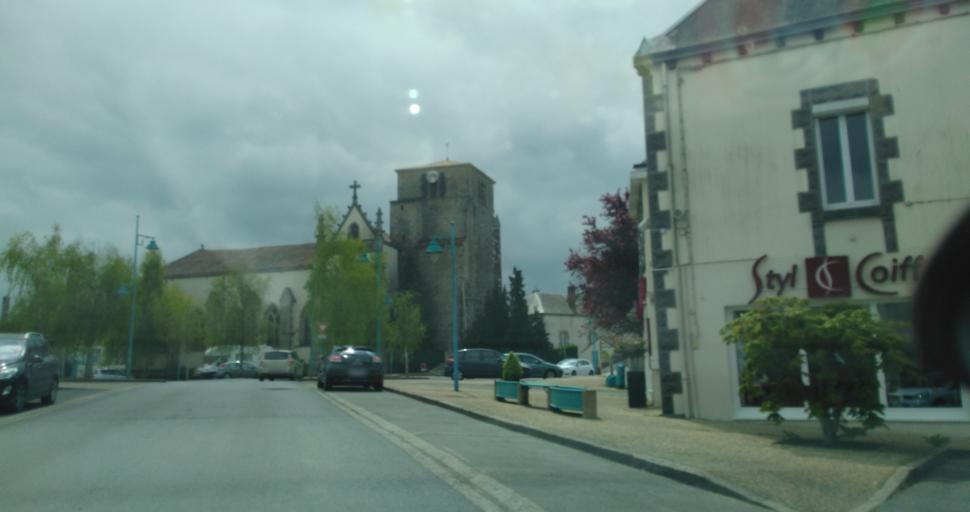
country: FR
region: Poitou-Charentes
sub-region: Departement des Deux-Sevres
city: Moncoutant
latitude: 46.7233
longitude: -0.5877
